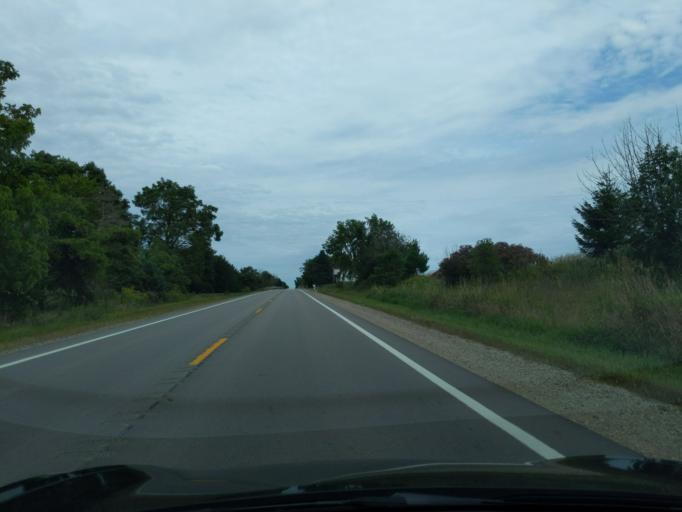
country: US
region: Michigan
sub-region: Barry County
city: Nashville
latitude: 42.5672
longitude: -85.0434
